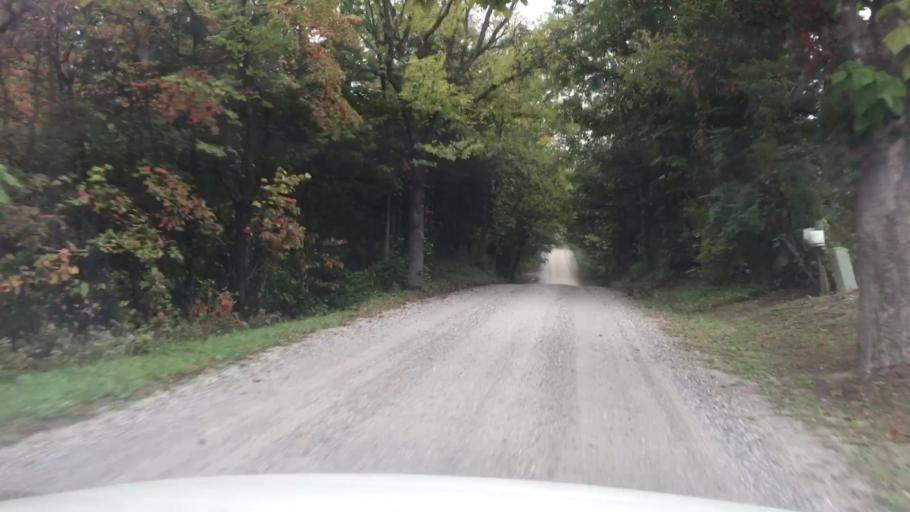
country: US
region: Missouri
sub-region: Boone County
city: Ashland
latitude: 38.8188
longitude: -92.3156
